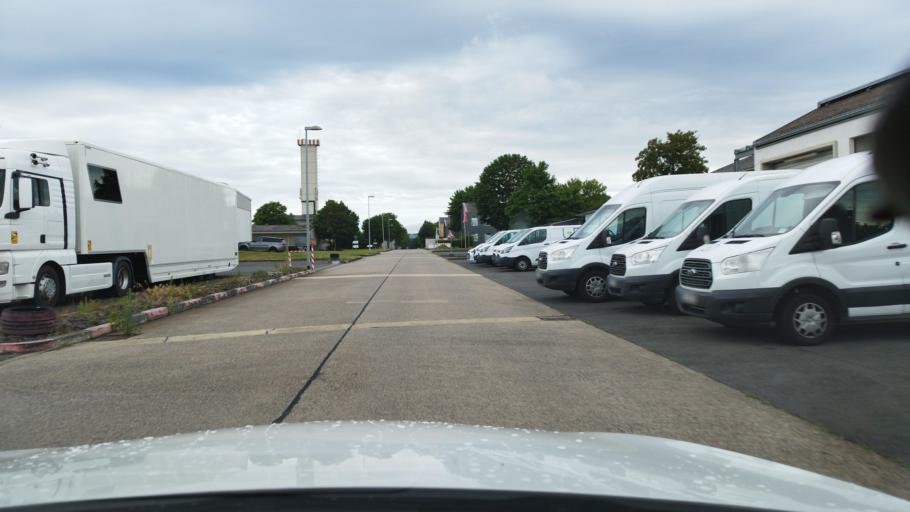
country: DE
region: Rheinland-Pfalz
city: Kruft
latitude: 50.3680
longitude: 7.3132
